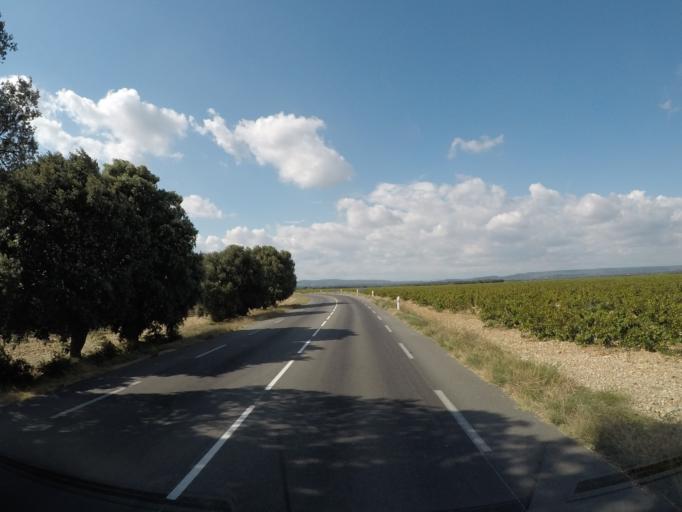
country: FR
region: Provence-Alpes-Cote d'Azur
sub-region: Departement du Vaucluse
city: Sainte-Cecile-les-Vignes
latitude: 44.2833
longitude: 4.8869
